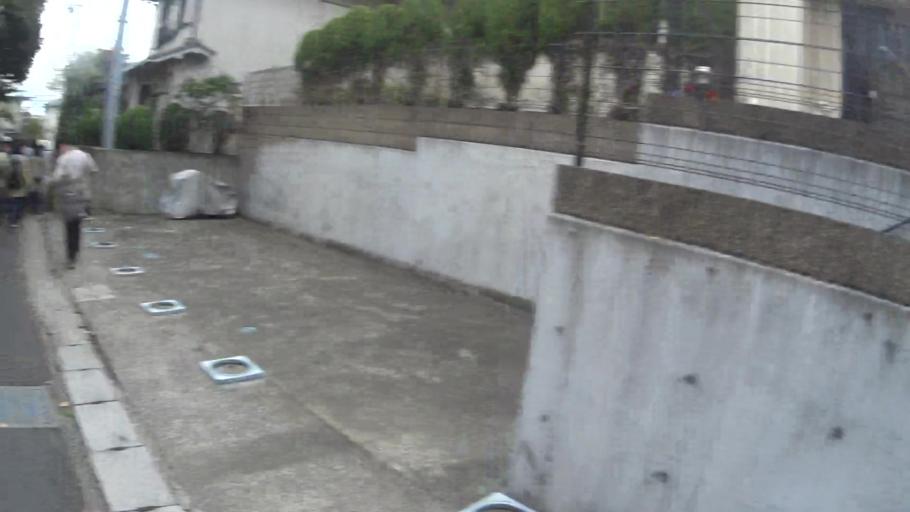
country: JP
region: Kanagawa
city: Fujisawa
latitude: 35.3115
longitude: 139.4918
